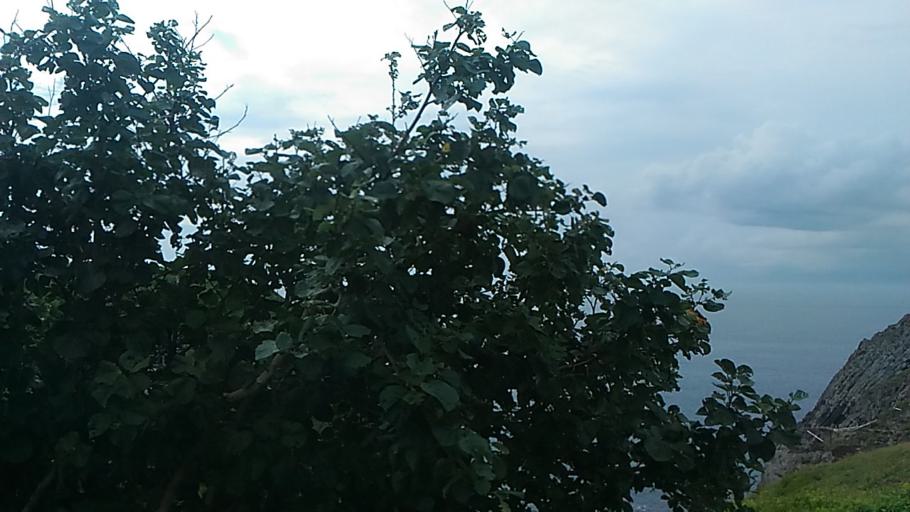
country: TW
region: Taiwan
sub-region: Penghu
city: Ma-kung
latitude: 23.1997
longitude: 119.4315
